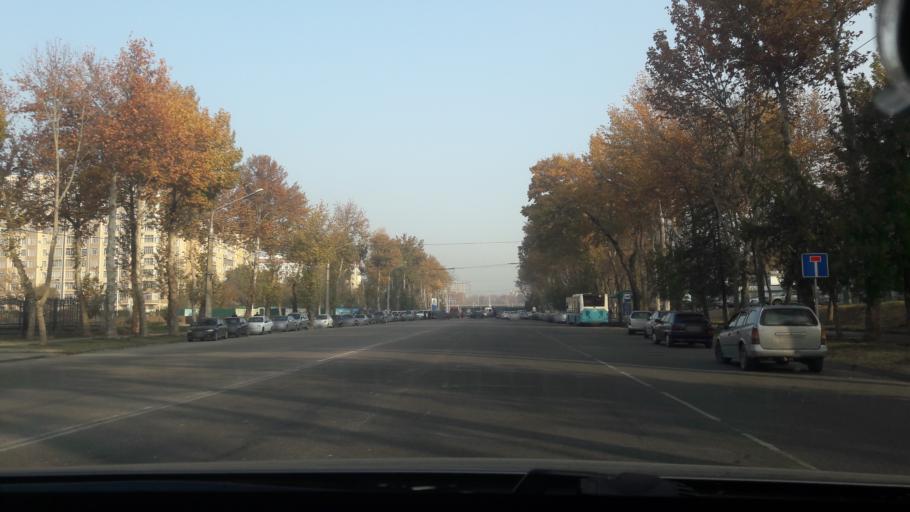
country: TJ
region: Dushanbe
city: Dushanbe
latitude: 38.5790
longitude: 68.7550
